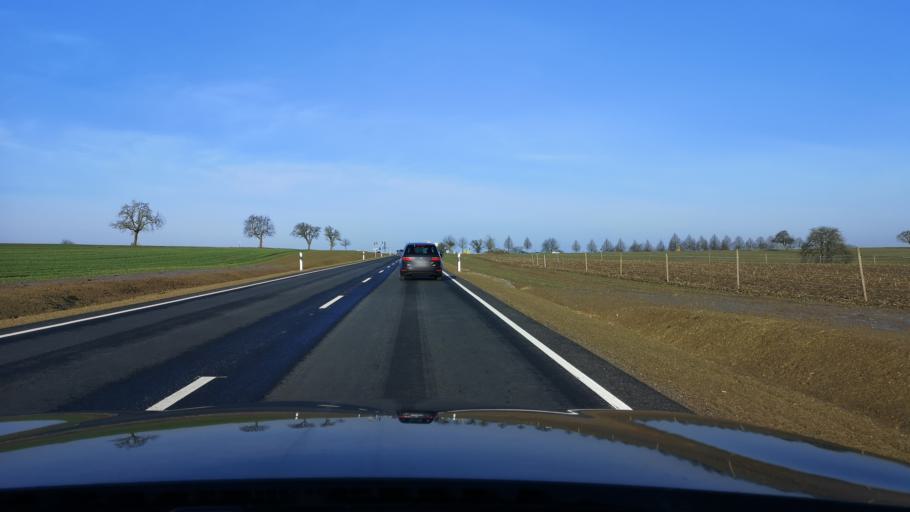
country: DE
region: Baden-Wuerttemberg
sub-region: Karlsruhe Region
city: Ettlingen
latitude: 48.9378
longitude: 8.4917
